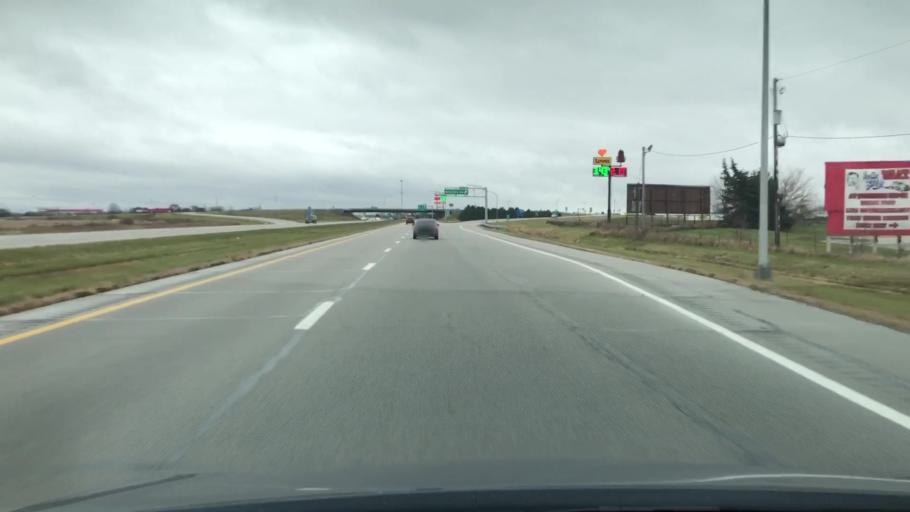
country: US
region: Ohio
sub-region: Wood County
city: Millbury
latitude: 41.5412
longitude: -83.4626
